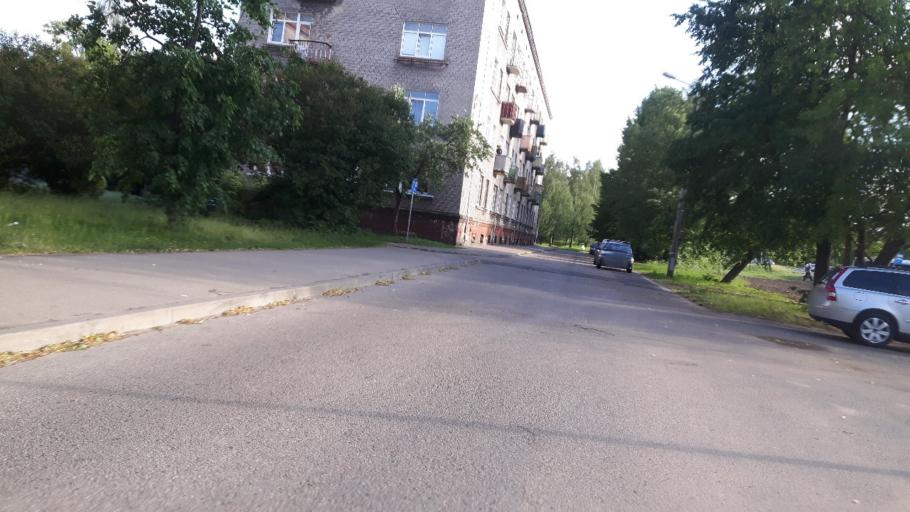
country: LV
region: Riga
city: Jaunciems
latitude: 57.0196
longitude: 24.1332
